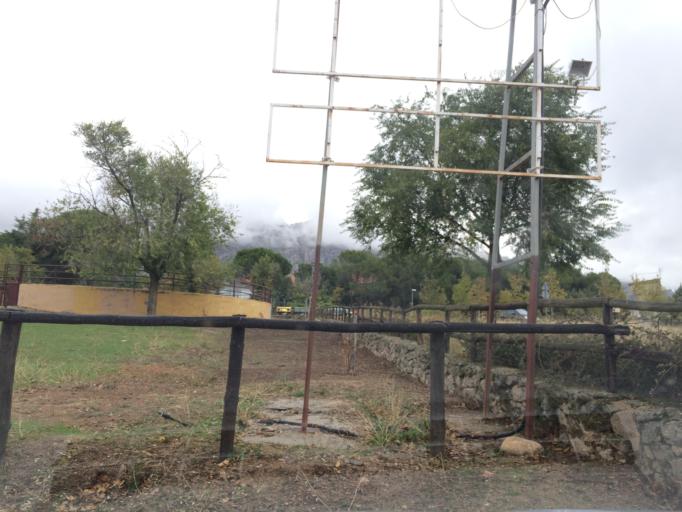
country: ES
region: Madrid
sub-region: Provincia de Madrid
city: Manzanares el Real
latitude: 40.7260
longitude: -3.8767
